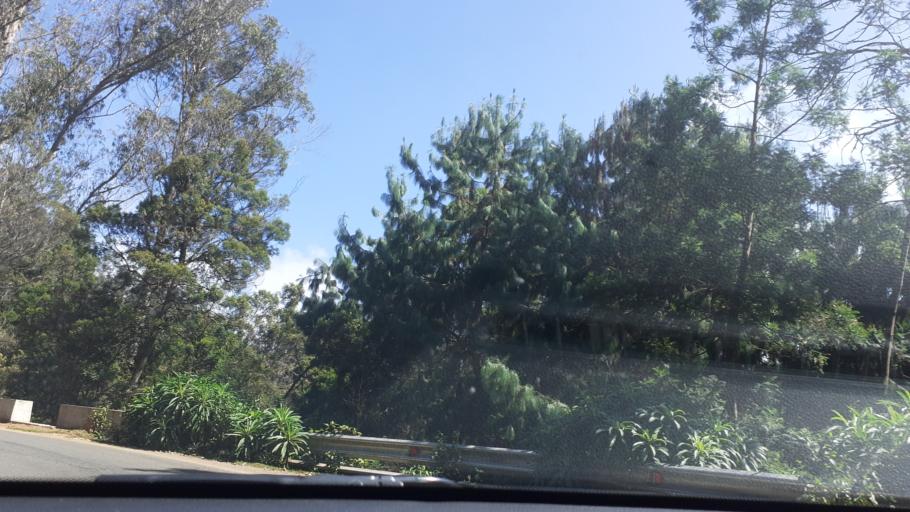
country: IN
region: Tamil Nadu
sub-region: Dindigul
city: Kodaikanal
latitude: 10.2203
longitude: 77.4207
